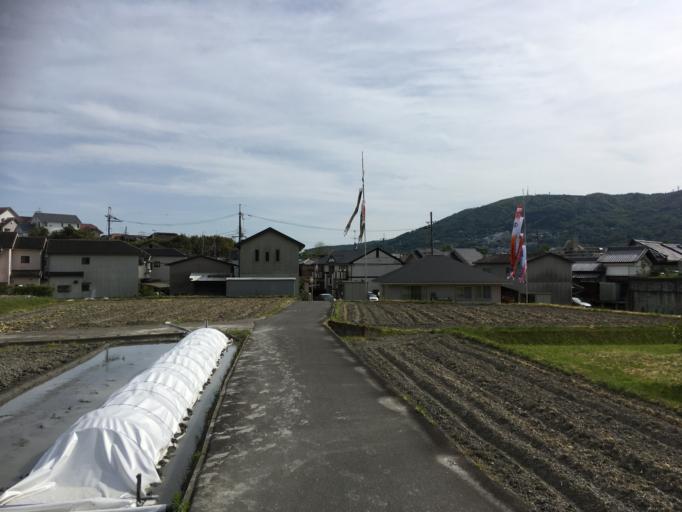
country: JP
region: Nara
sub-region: Ikoma-shi
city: Ikoma
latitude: 34.7053
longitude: 135.7097
